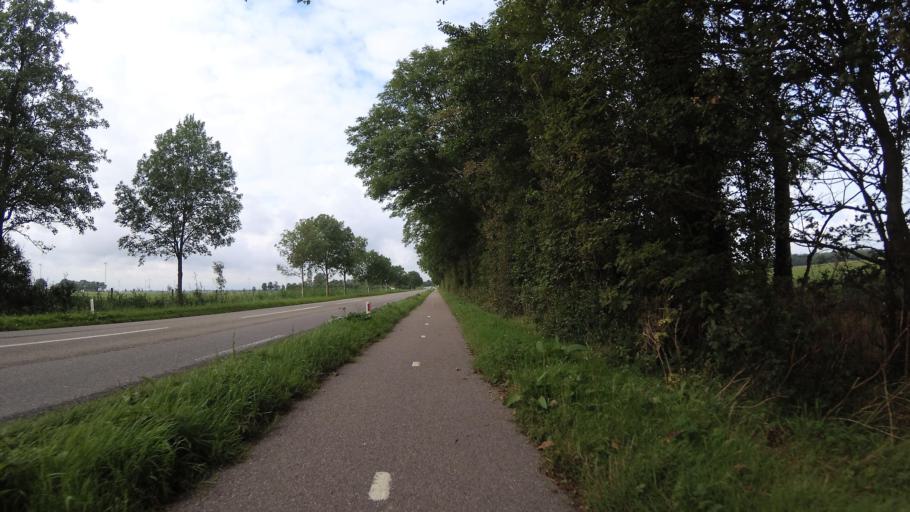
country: NL
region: North Holland
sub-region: Gemeente Hollands Kroon
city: Den Oever
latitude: 52.8448
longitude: 4.9578
